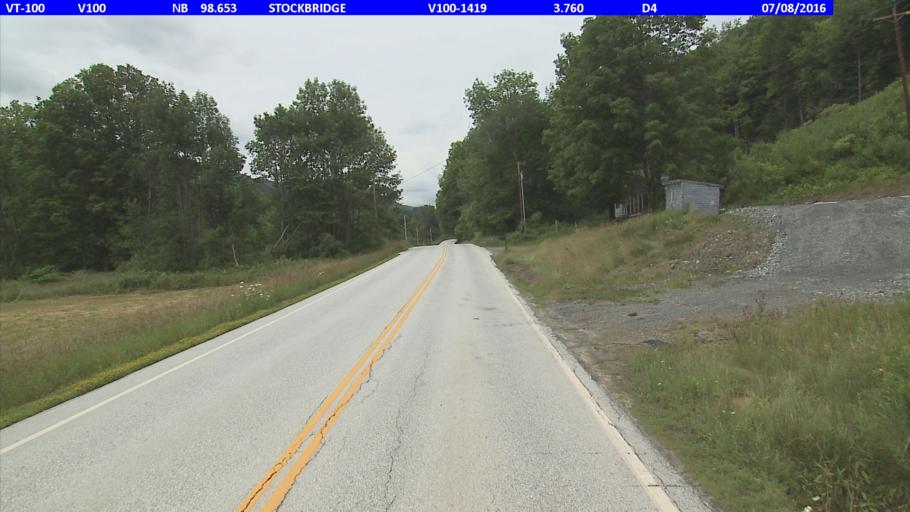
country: US
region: Vermont
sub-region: Orange County
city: Randolph
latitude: 43.7922
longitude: -72.7634
